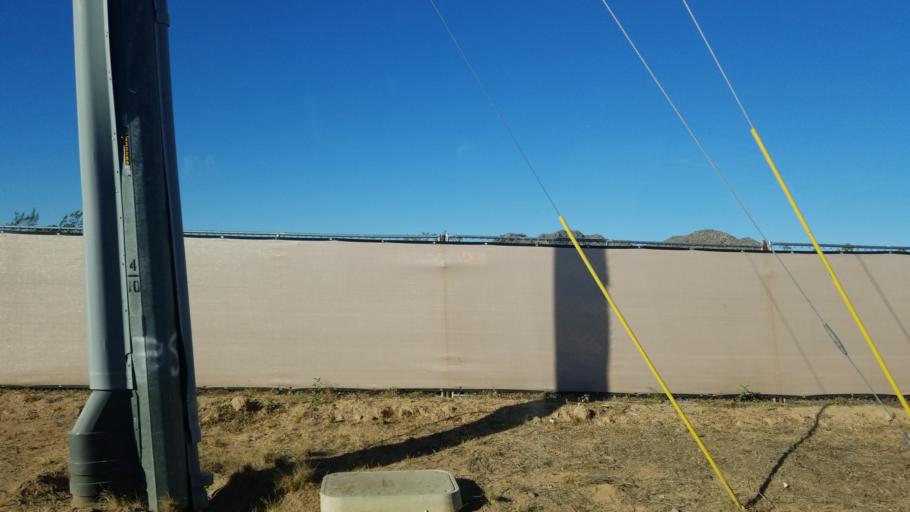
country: US
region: Arizona
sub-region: Maricopa County
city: Paradise Valley
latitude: 33.5376
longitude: -111.9259
